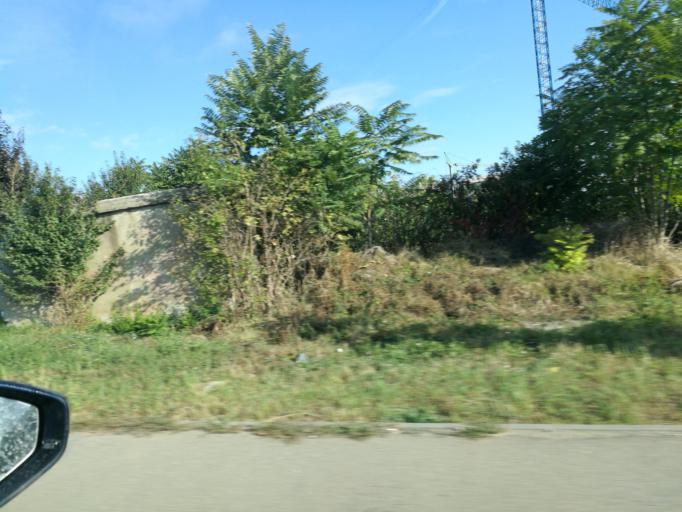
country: RO
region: Bihor
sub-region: Comuna Biharea
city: Oradea
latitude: 47.0413
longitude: 21.9252
